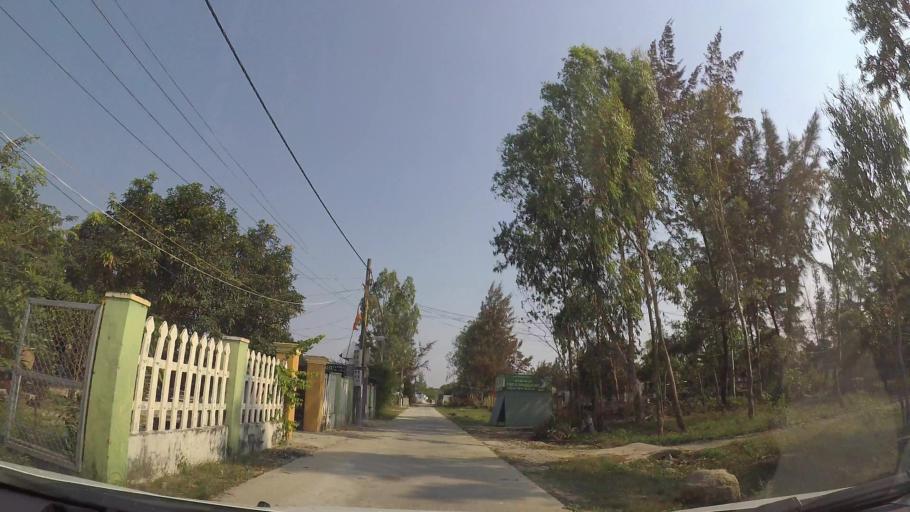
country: VN
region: Quang Nam
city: Quang Nam
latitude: 15.9477
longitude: 108.2703
